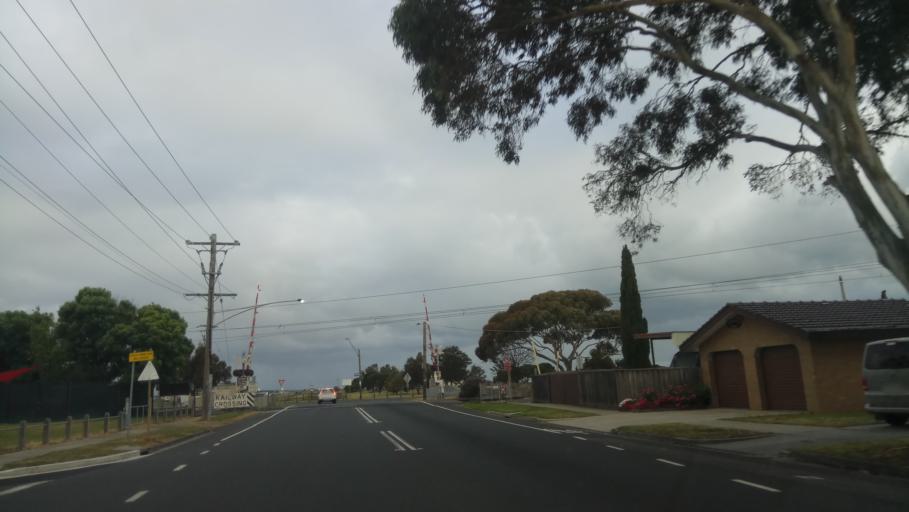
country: AU
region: Victoria
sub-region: Hobsons Bay
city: Seaholme
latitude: -37.8659
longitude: 144.8437
